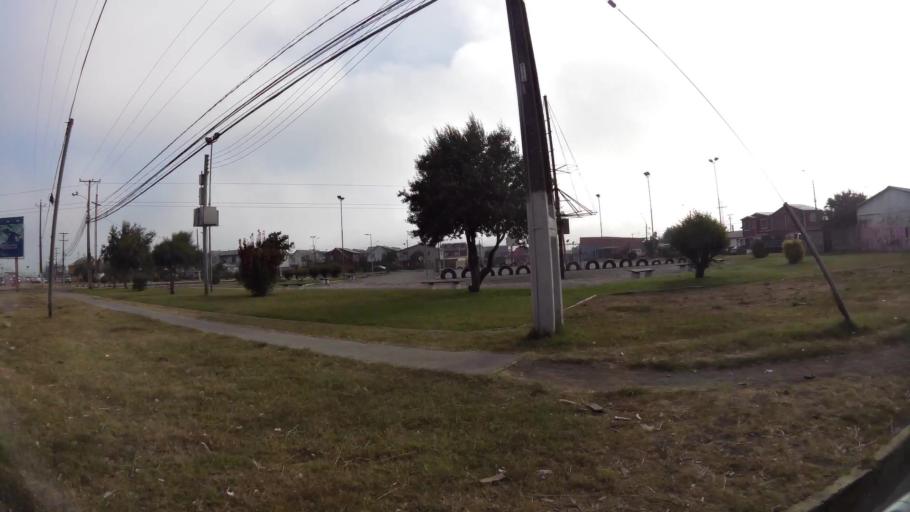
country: CL
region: Biobio
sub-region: Provincia de Concepcion
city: Concepcion
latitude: -36.8015
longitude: -73.1055
